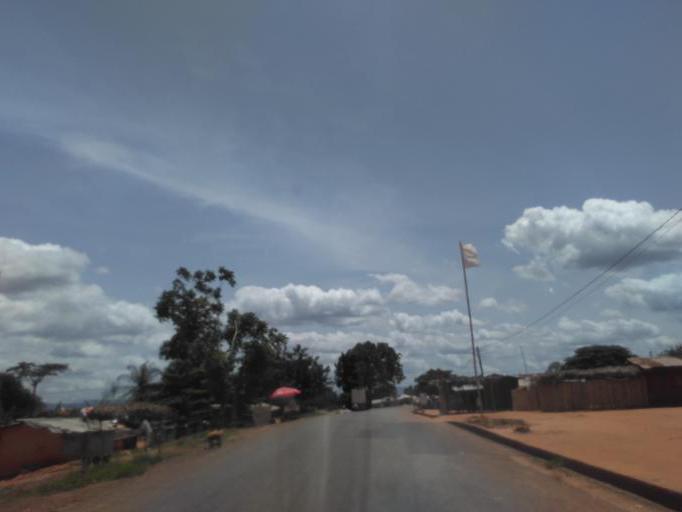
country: GH
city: Akropong
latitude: 6.0628
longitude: -0.0981
